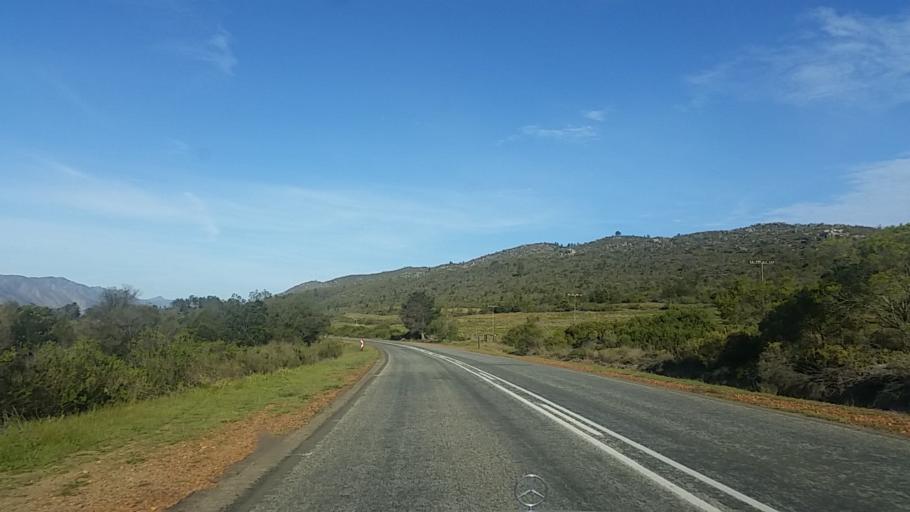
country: ZA
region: Western Cape
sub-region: Eden District Municipality
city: Knysna
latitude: -33.7746
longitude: 22.9046
